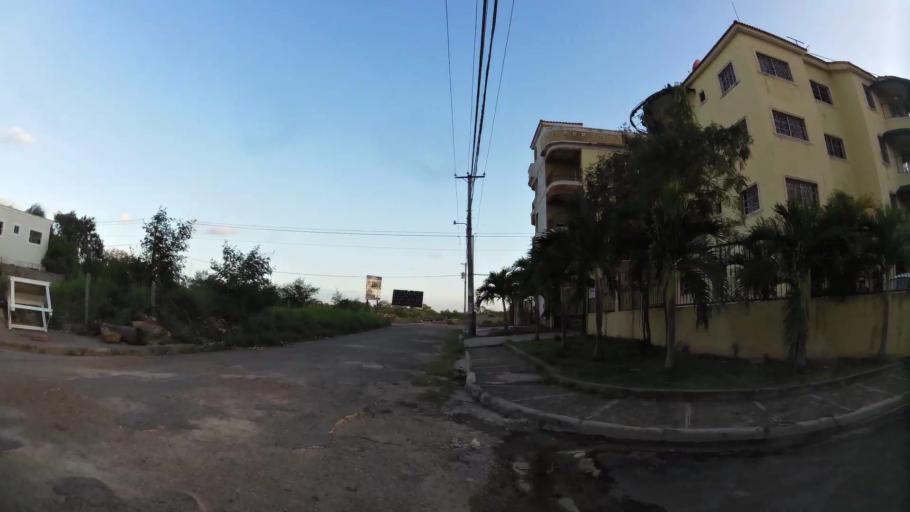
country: DO
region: Santo Domingo
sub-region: Santo Domingo
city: Santo Domingo Este
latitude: 18.4869
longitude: -69.8196
